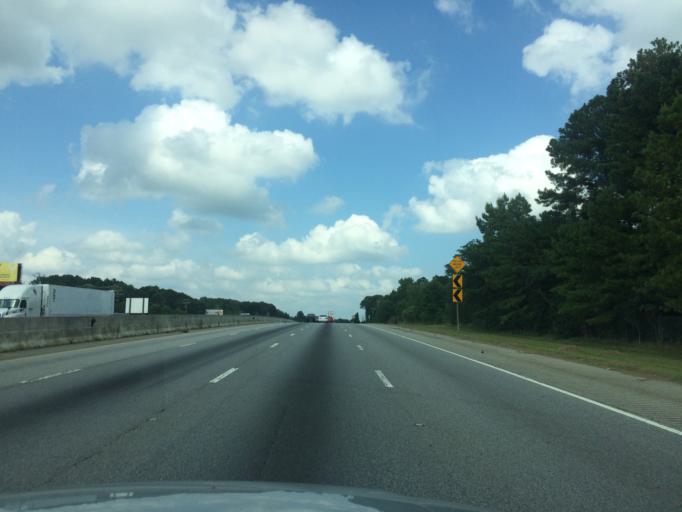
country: US
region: South Carolina
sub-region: Spartanburg County
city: Mayo
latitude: 35.0212
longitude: -81.8904
